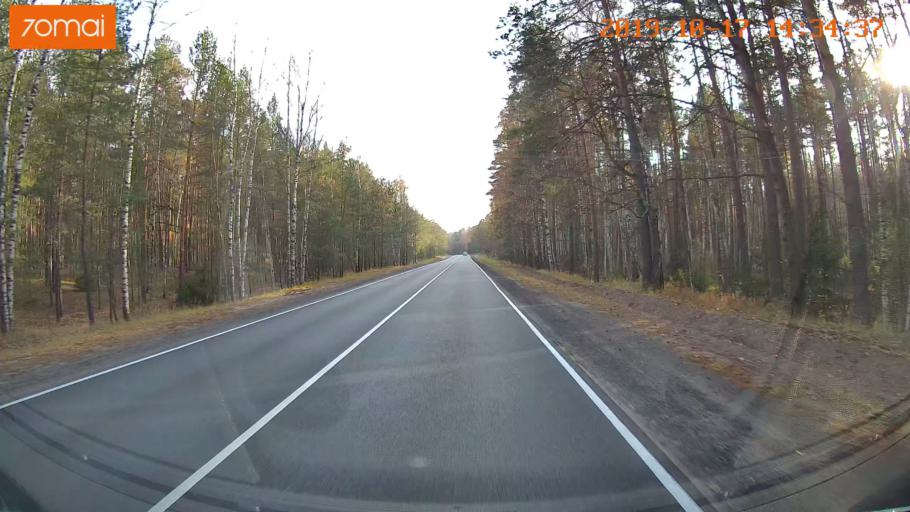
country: RU
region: Rjazan
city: Solotcha
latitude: 54.9100
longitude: 39.9982
